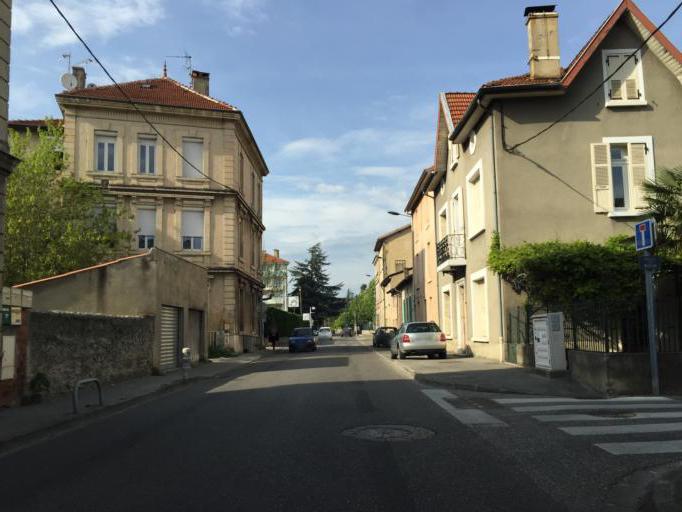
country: FR
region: Rhone-Alpes
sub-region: Departement de la Drome
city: Romans-sur-Isere
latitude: 45.0523
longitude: 5.0479
